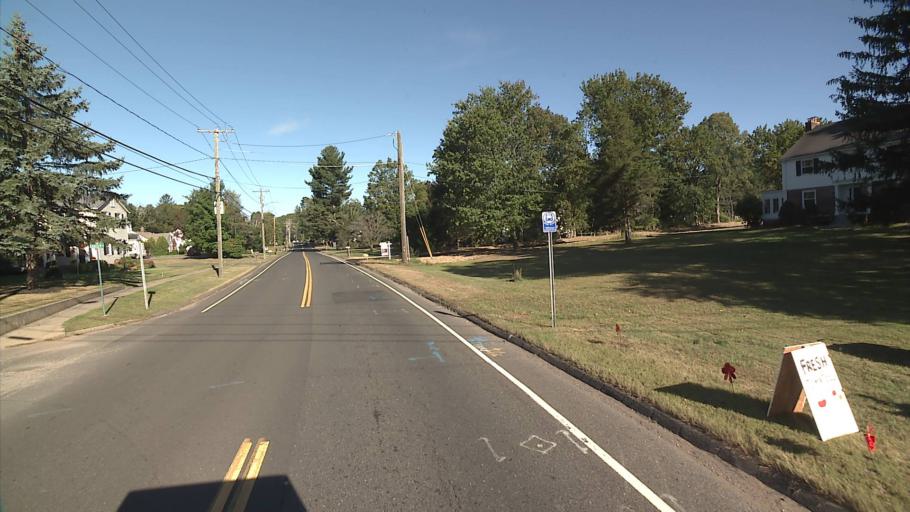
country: US
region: Connecticut
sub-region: New Haven County
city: Cheshire Village
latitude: 41.5111
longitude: -72.9181
